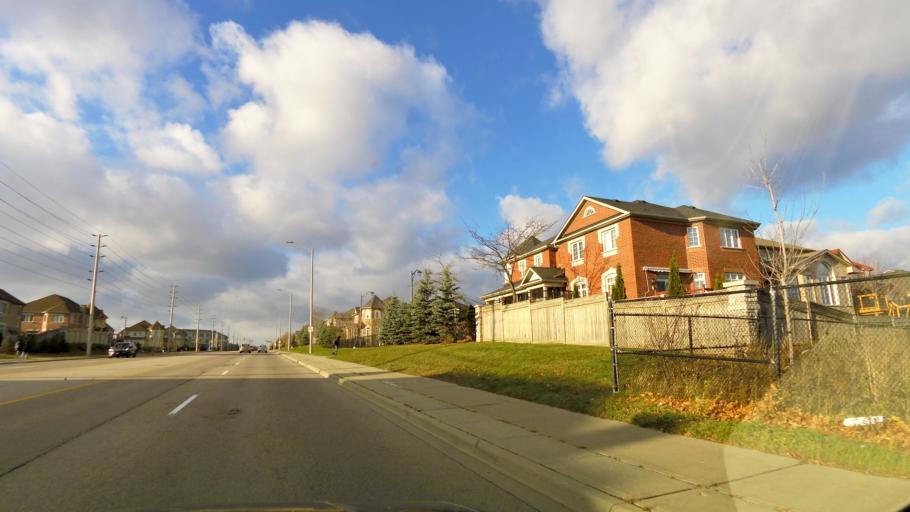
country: CA
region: Ontario
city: Mississauga
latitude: 43.6305
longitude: -79.7086
